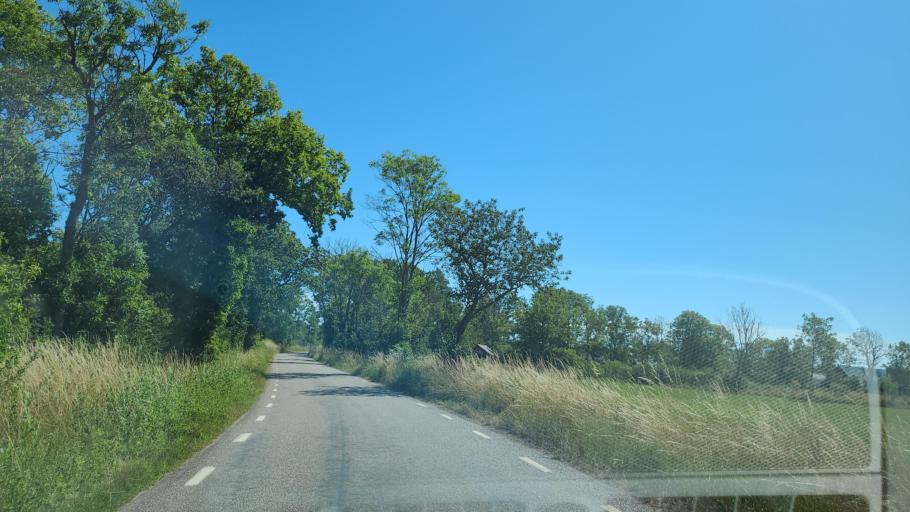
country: SE
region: Kalmar
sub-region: Borgholms Kommun
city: Borgholm
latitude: 56.7453
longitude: 16.6641
